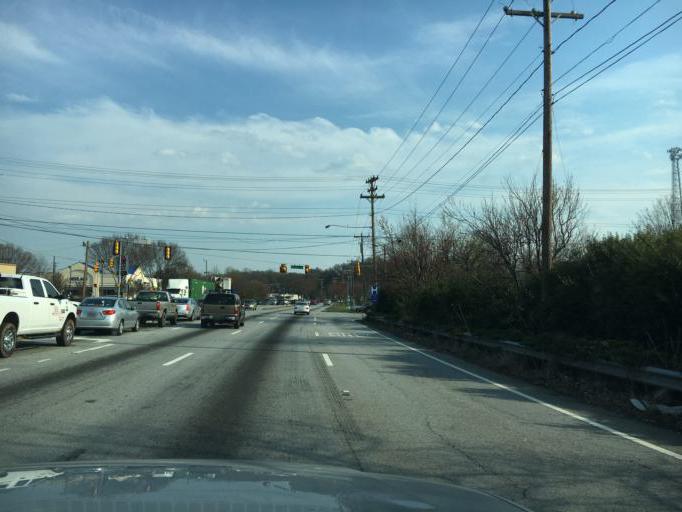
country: US
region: South Carolina
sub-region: Spartanburg County
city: Spartanburg
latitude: 34.9685
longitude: -81.9343
